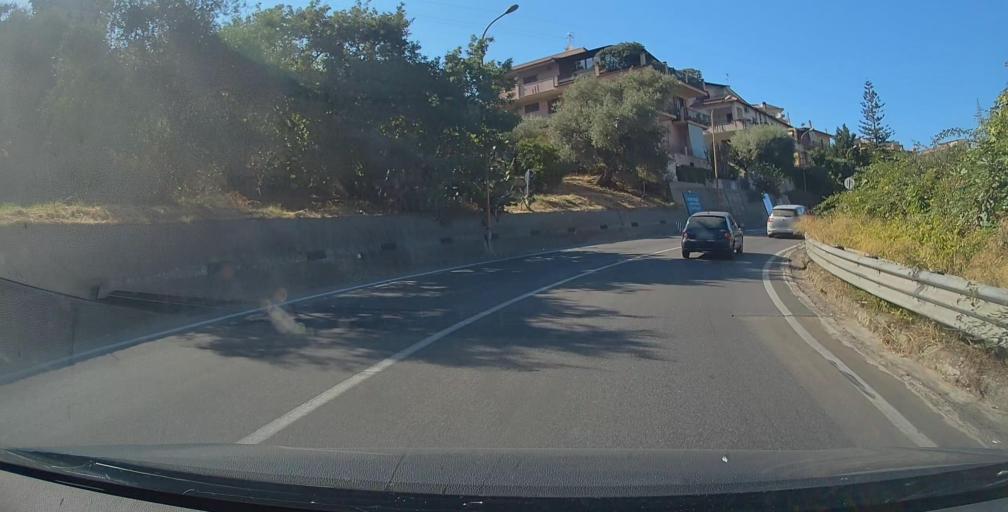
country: IT
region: Sicily
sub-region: Messina
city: Capo d'Orlando
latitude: 38.1542
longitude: 14.7524
